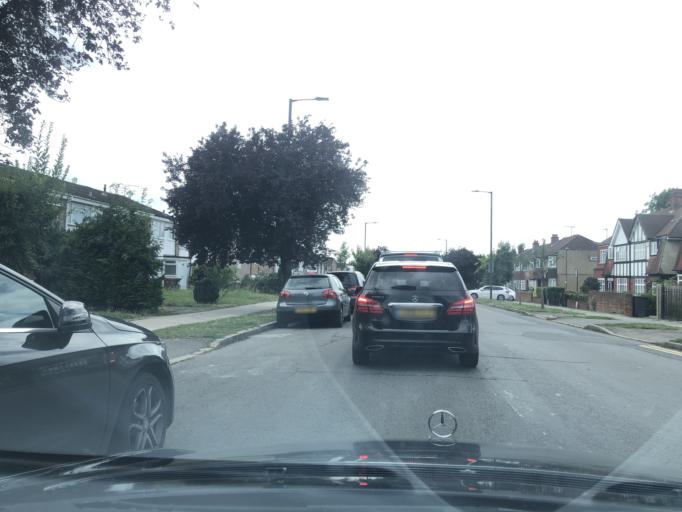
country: GB
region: England
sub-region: Greater London
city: Northolt
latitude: 51.5636
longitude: -0.3667
